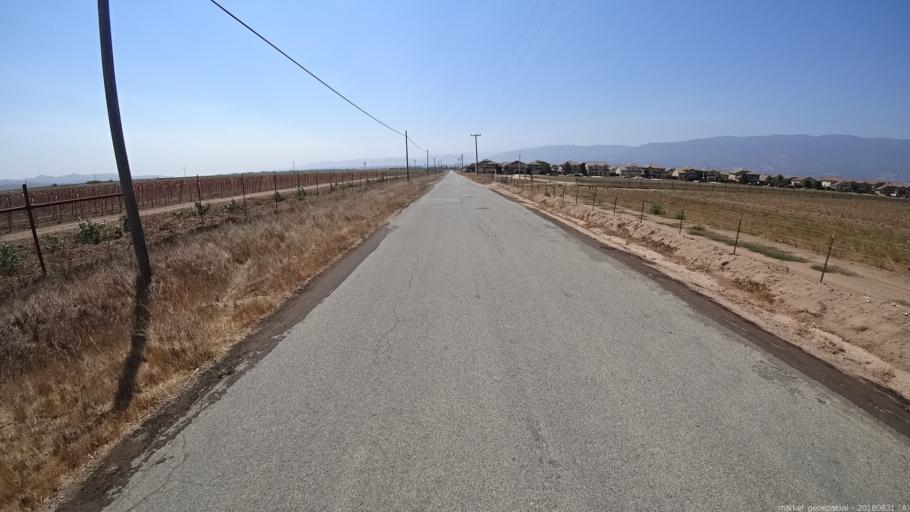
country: US
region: California
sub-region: Monterey County
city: Soledad
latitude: 36.4419
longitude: -121.3119
